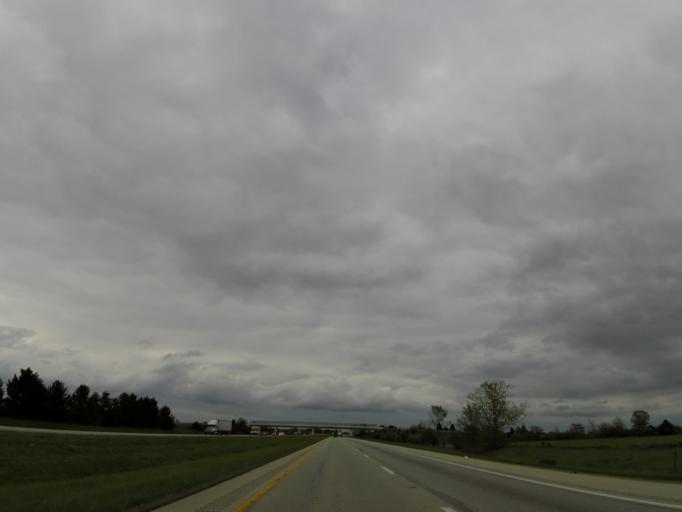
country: US
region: Ohio
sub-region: Greene County
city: Jamestown
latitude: 39.5640
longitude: -83.7079
